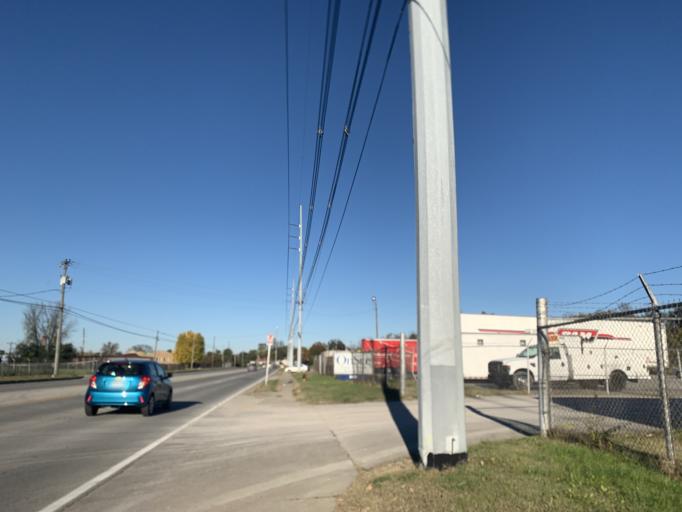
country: US
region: Kentucky
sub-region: Jefferson County
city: Shively
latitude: 38.2010
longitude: -85.7942
